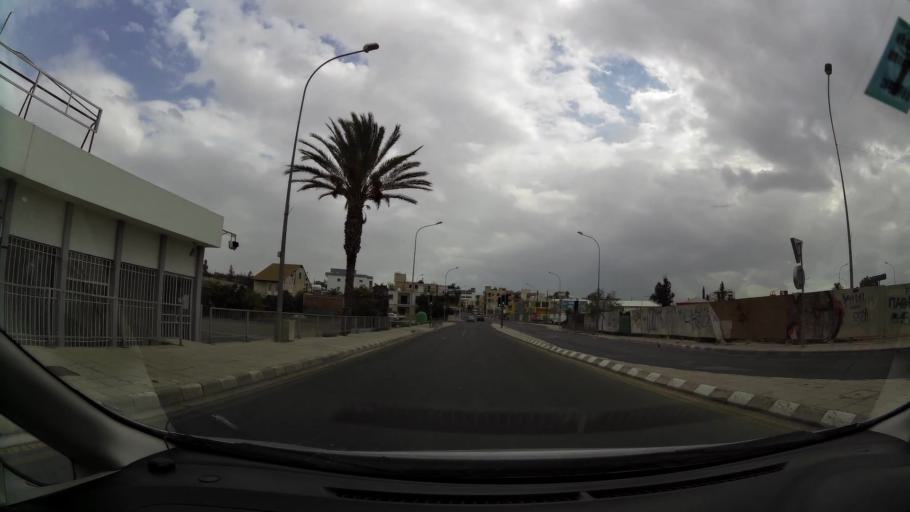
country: CY
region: Lefkosia
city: Geri
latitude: 35.1180
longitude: 33.3778
